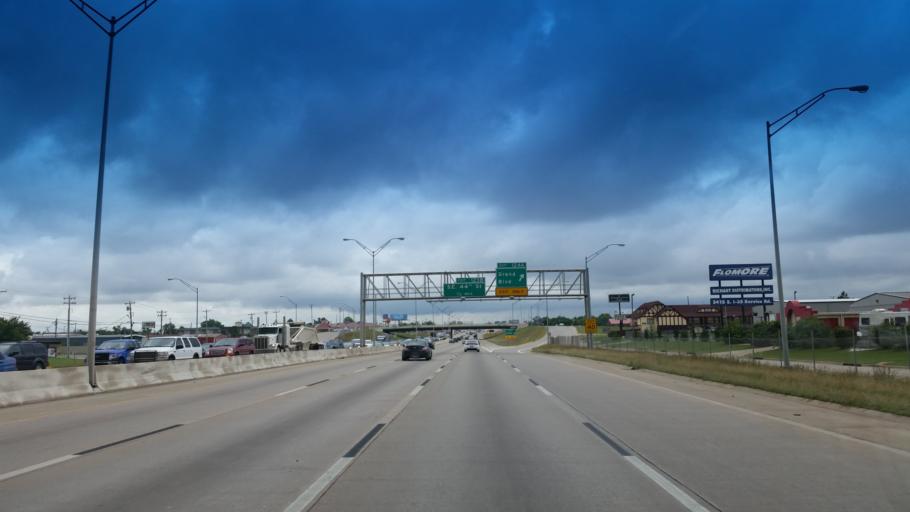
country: US
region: Oklahoma
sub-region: Oklahoma County
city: Del City
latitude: 35.4317
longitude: -97.4863
